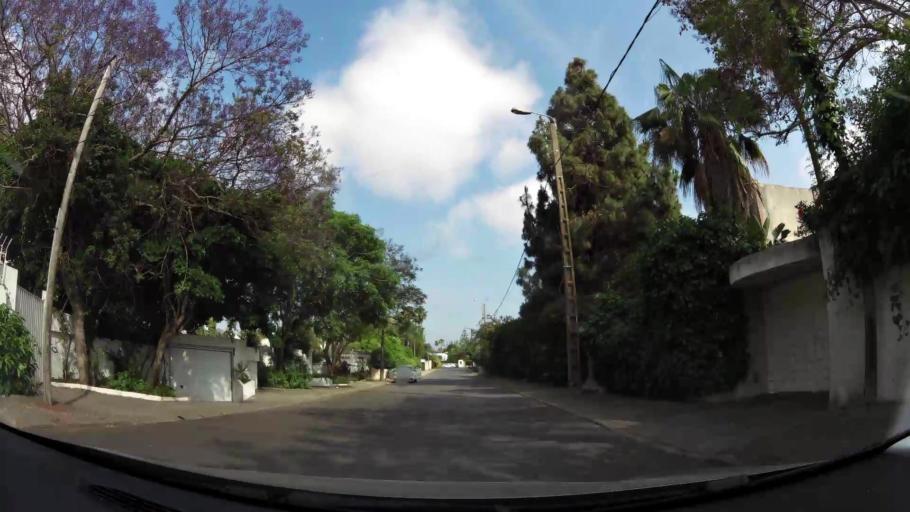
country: MA
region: Rabat-Sale-Zemmour-Zaer
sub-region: Rabat
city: Rabat
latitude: 33.9692
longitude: -6.8577
